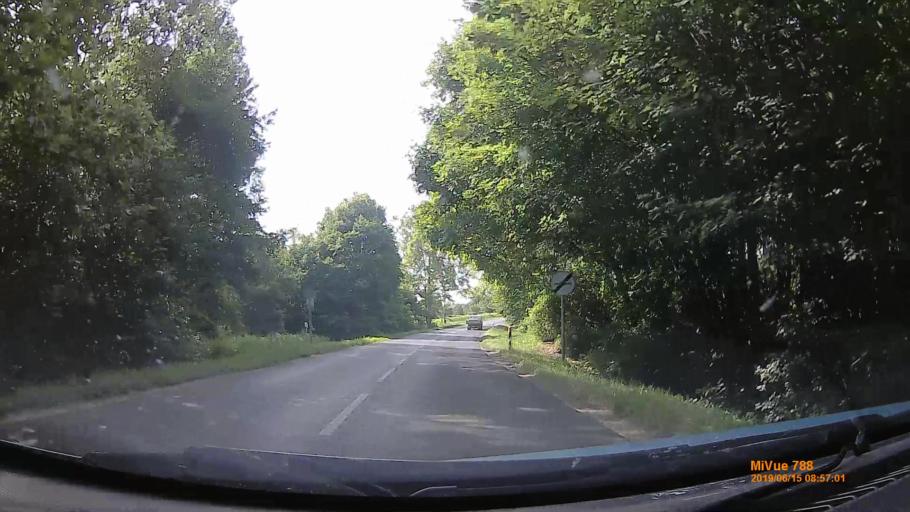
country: HU
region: Somogy
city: Adand
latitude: 46.8123
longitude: 18.1375
